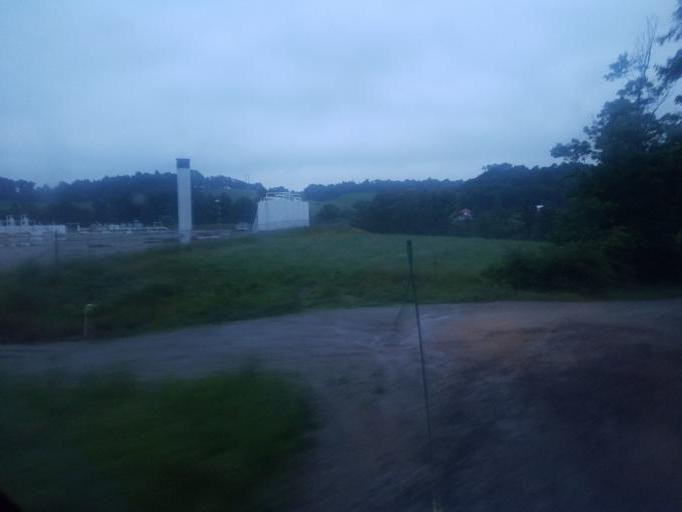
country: US
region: Ohio
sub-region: Carroll County
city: Carrollton
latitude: 40.5039
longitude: -81.0527
